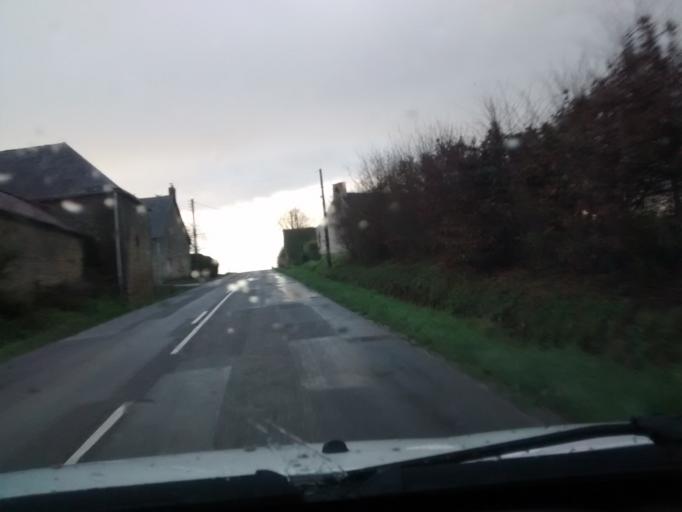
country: FR
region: Brittany
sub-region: Departement d'Ille-et-Vilaine
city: Bais
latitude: 47.9909
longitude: -1.2863
